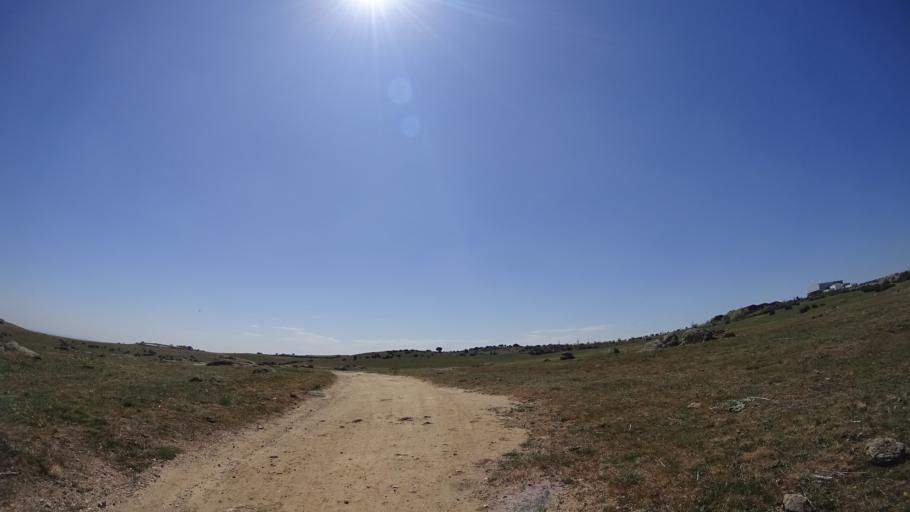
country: ES
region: Madrid
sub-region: Provincia de Madrid
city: Colmenar Viejo
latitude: 40.6968
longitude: -3.7564
